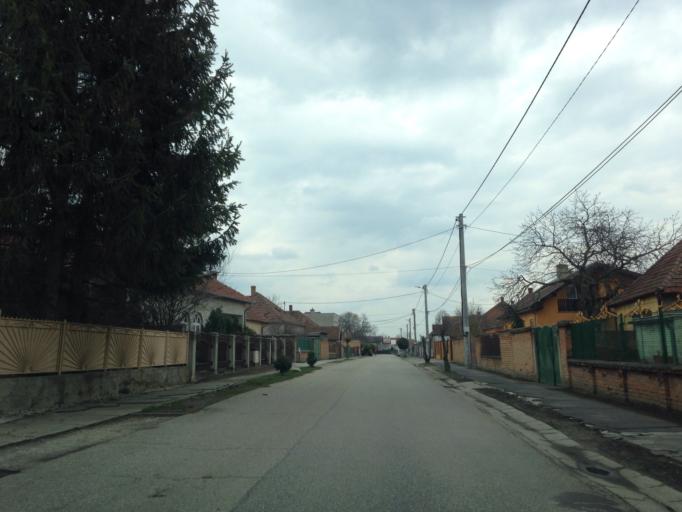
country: SK
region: Nitriansky
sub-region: Okres Nove Zamky
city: Nove Zamky
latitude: 47.9965
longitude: 18.2669
